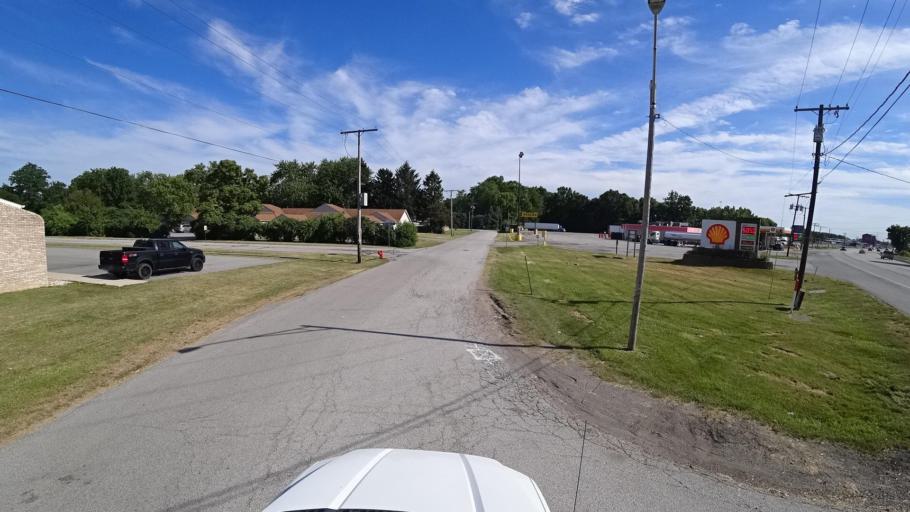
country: US
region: Indiana
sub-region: Porter County
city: Porter
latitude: 41.6138
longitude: -87.0951
